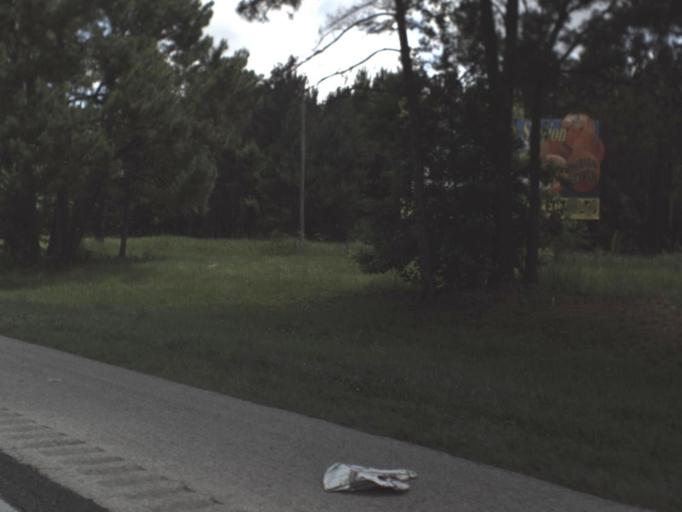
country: US
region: Florida
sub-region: Alachua County
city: High Springs
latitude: 29.8639
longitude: -82.5406
